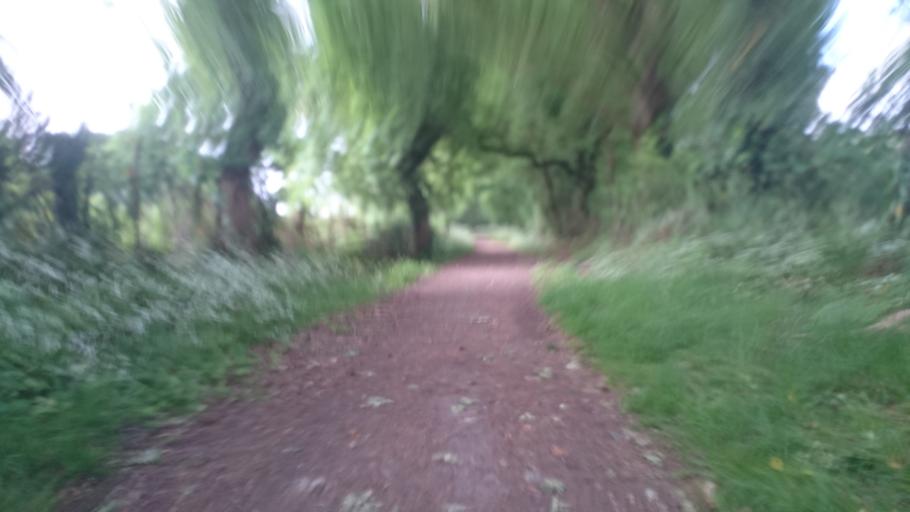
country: FR
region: Pays de la Loire
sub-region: Departement de la Loire-Atlantique
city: La Montagne
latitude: 47.1814
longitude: -1.6655
